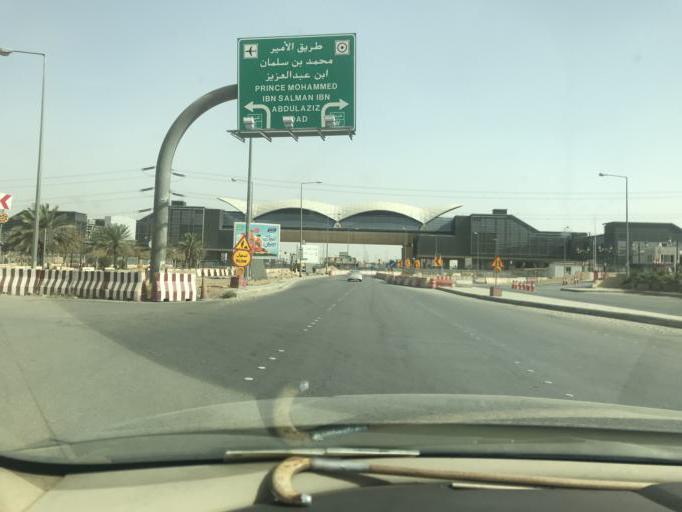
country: SA
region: Ar Riyad
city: Riyadh
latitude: 24.8031
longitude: 46.6951
